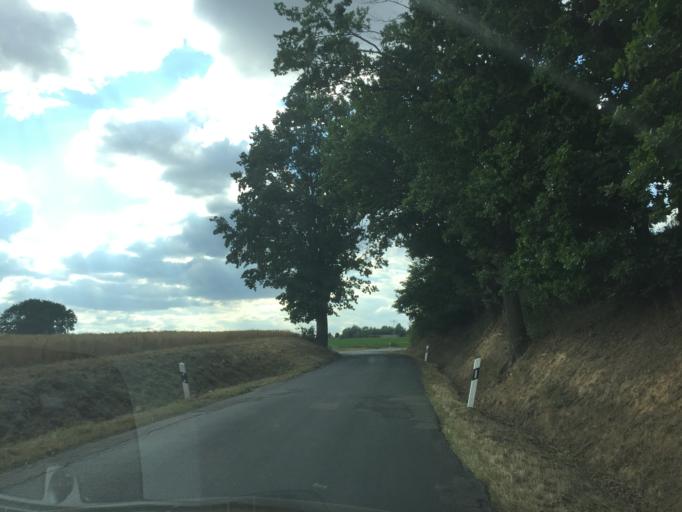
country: DE
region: Thuringia
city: Altenburg
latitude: 50.9601
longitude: 12.4417
